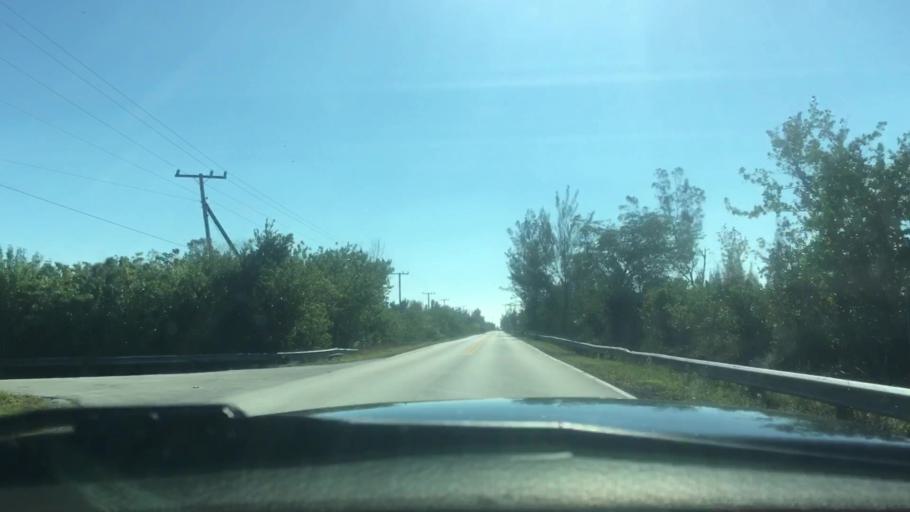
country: US
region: Florida
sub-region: Miami-Dade County
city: Florida City
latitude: 25.3727
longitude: -80.4336
